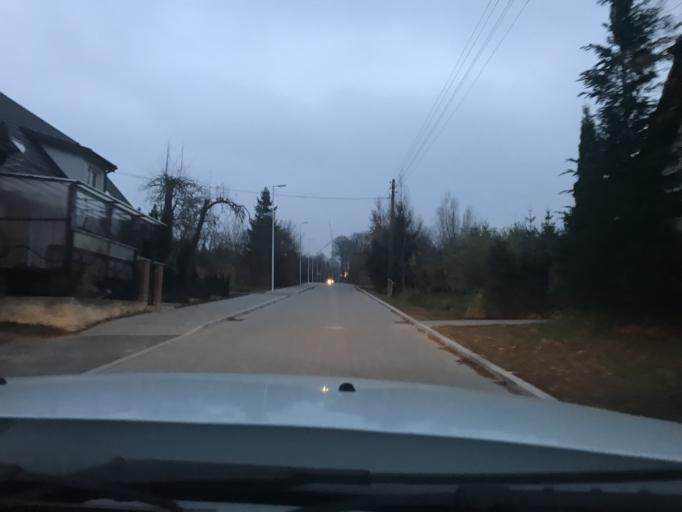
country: PL
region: West Pomeranian Voivodeship
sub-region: Powiat slawienski
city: Darlowo
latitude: 54.4803
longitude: 16.5090
